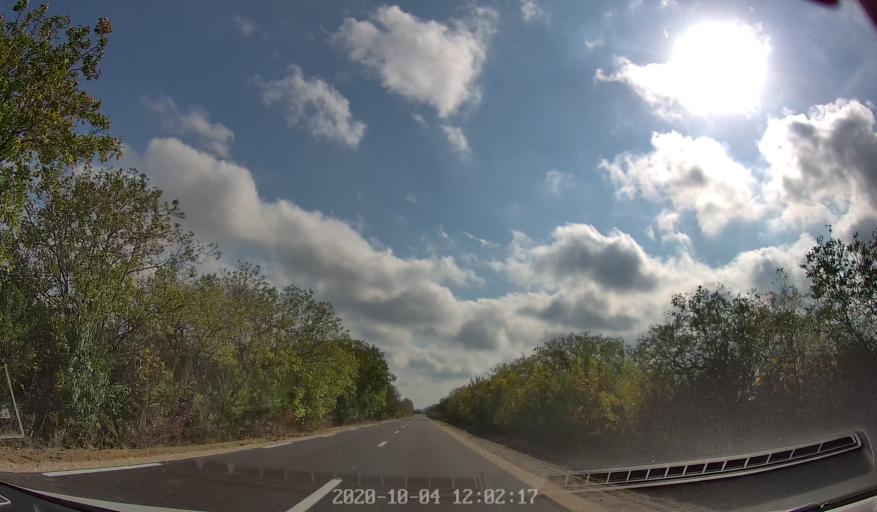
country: MD
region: Rezina
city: Saharna
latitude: 47.6182
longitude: 28.9042
